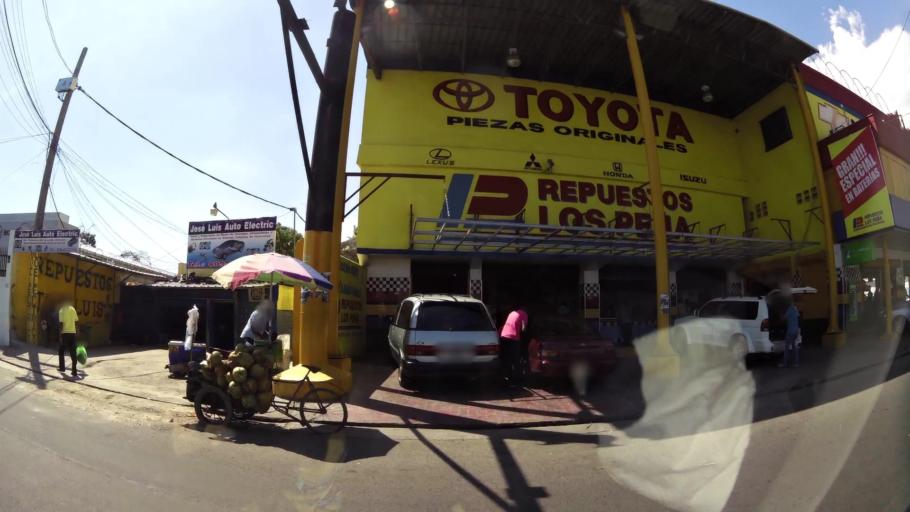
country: DO
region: Nacional
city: Bella Vista
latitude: 18.4631
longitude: -69.9755
